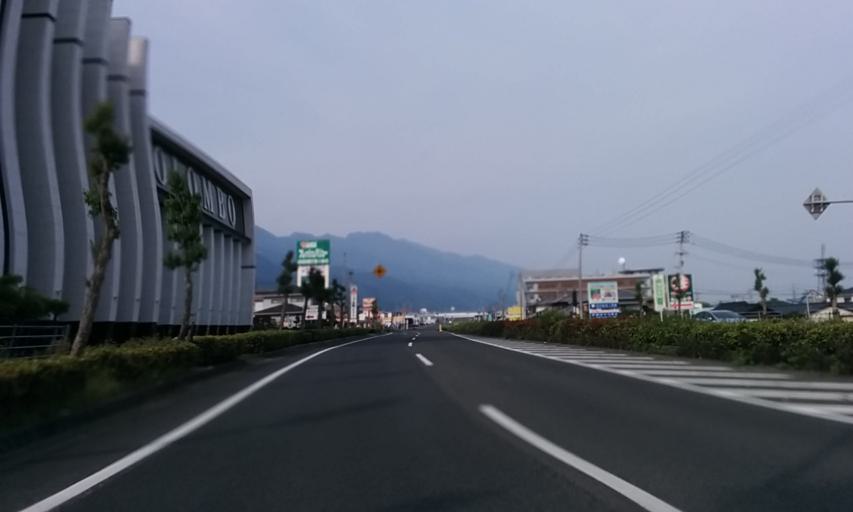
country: JP
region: Ehime
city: Kawanoecho
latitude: 33.9799
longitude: 133.5528
